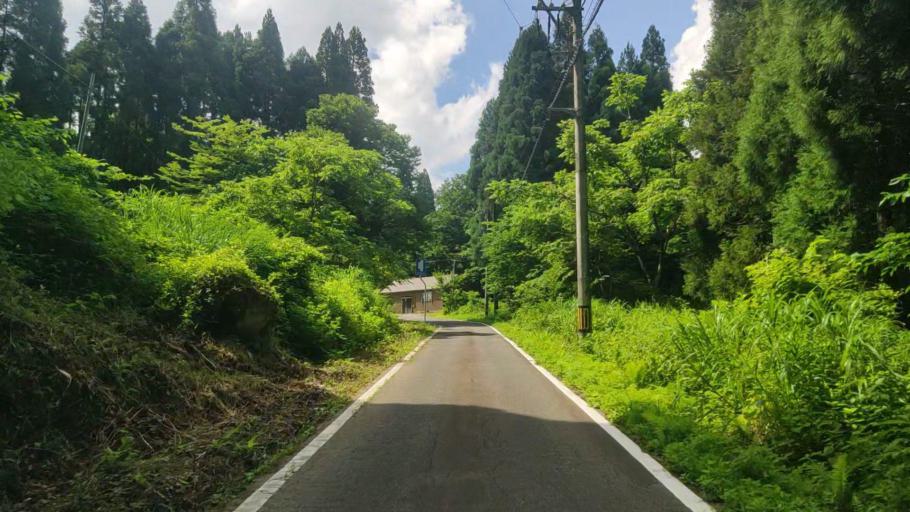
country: JP
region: Fukui
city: Katsuyama
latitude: 36.2189
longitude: 136.5303
